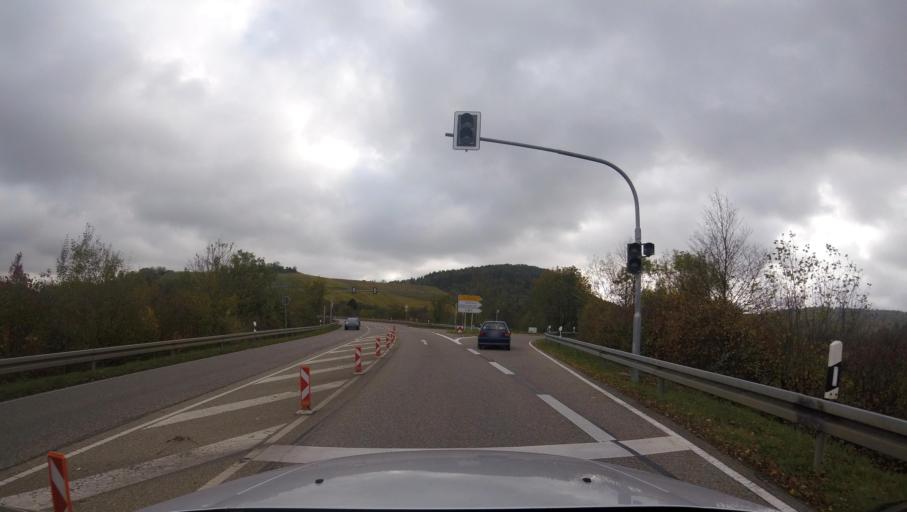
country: DE
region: Baden-Wuerttemberg
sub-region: Regierungsbezirk Stuttgart
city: Winnenden
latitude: 48.8645
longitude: 9.3923
